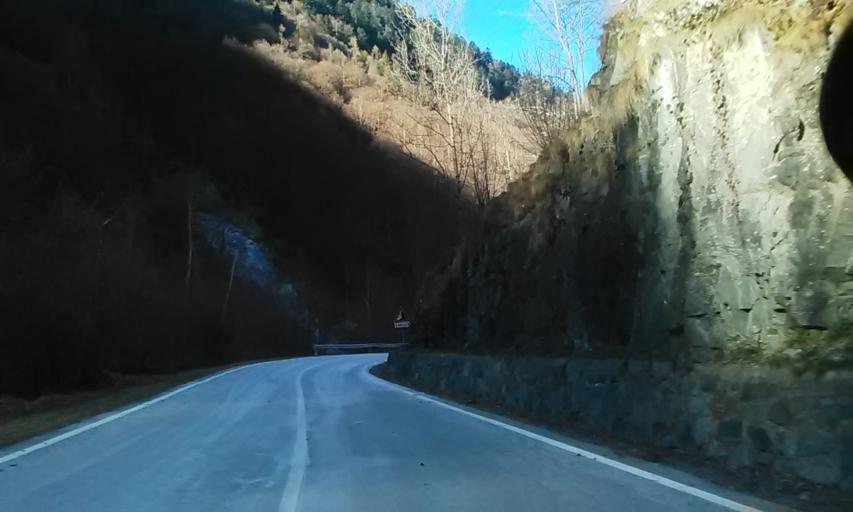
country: IT
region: Piedmont
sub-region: Provincia di Vercelli
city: Rimasco
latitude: 45.8774
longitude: 8.0679
